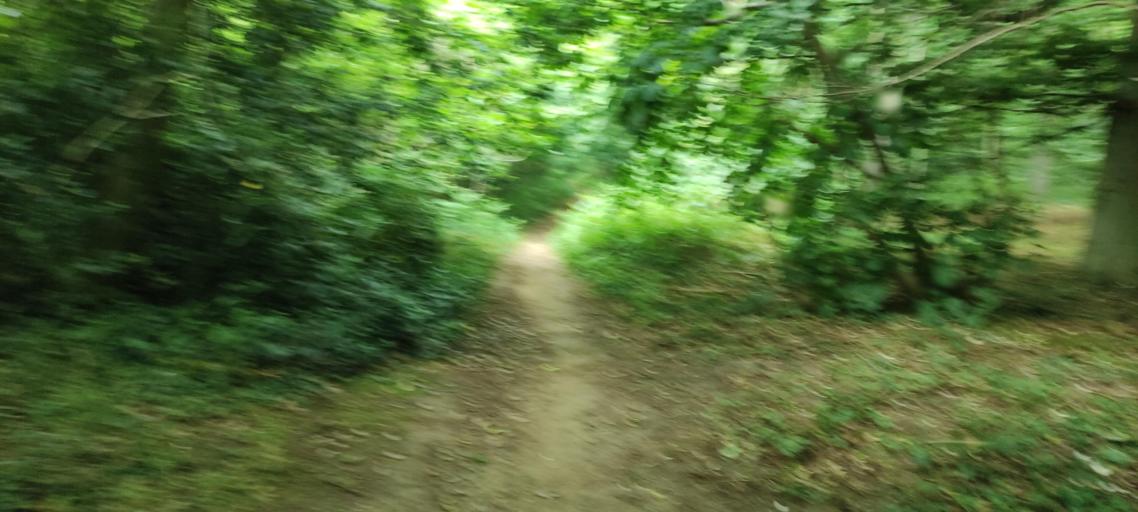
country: GB
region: England
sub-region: North Lincolnshire
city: Croxton
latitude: 53.5473
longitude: -0.3359
